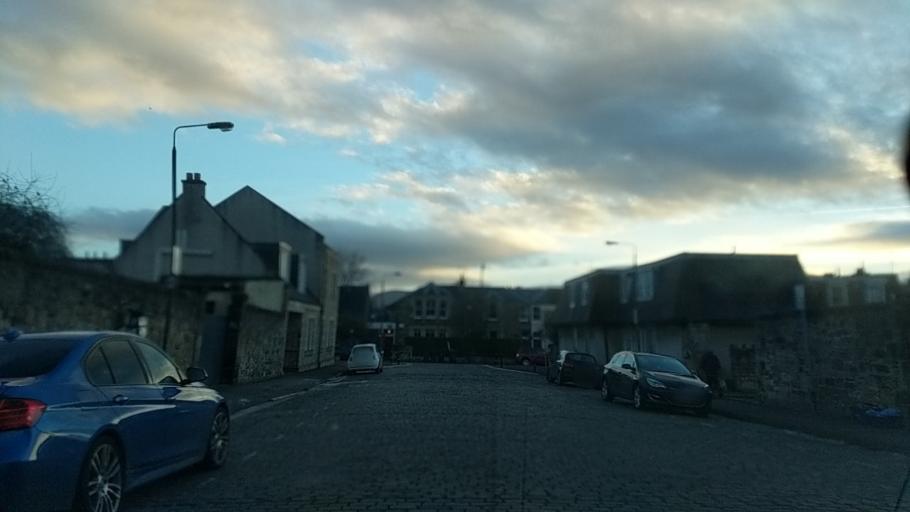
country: GB
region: Scotland
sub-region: Edinburgh
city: Edinburgh
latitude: 55.9455
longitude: -3.2275
